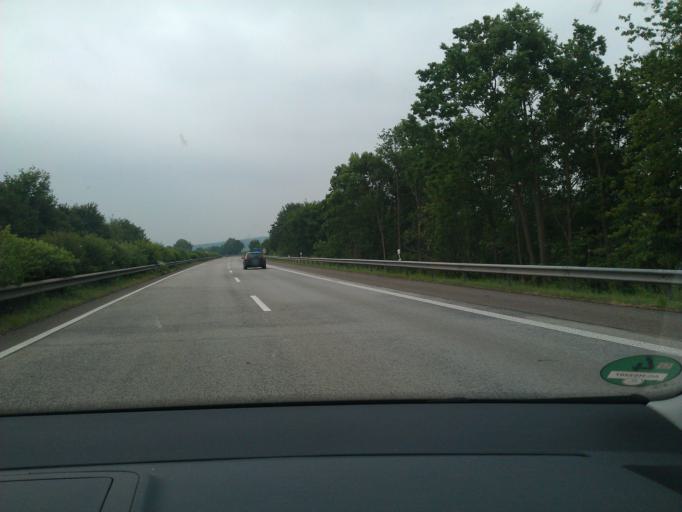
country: DE
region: Rheinland-Pfalz
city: Saffig
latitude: 50.3715
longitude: 7.4168
